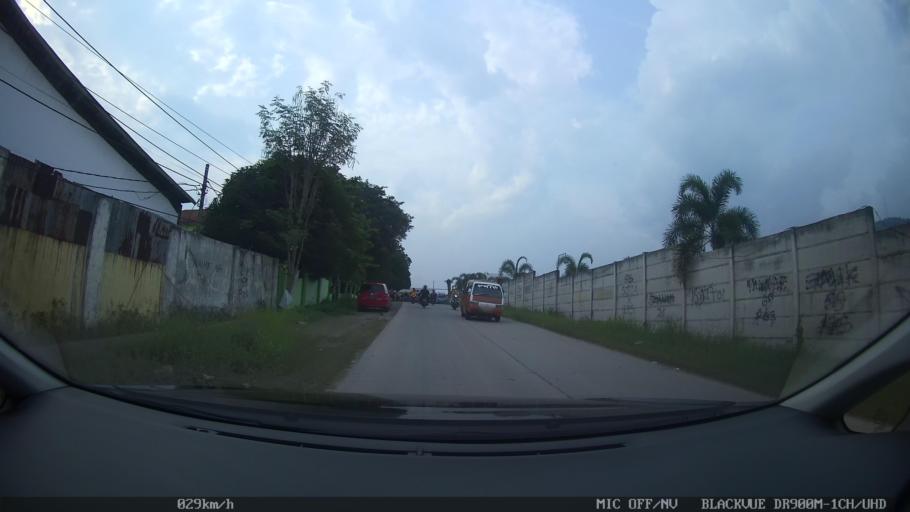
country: ID
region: Lampung
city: Bandarlampung
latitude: -5.4388
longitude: 105.2968
